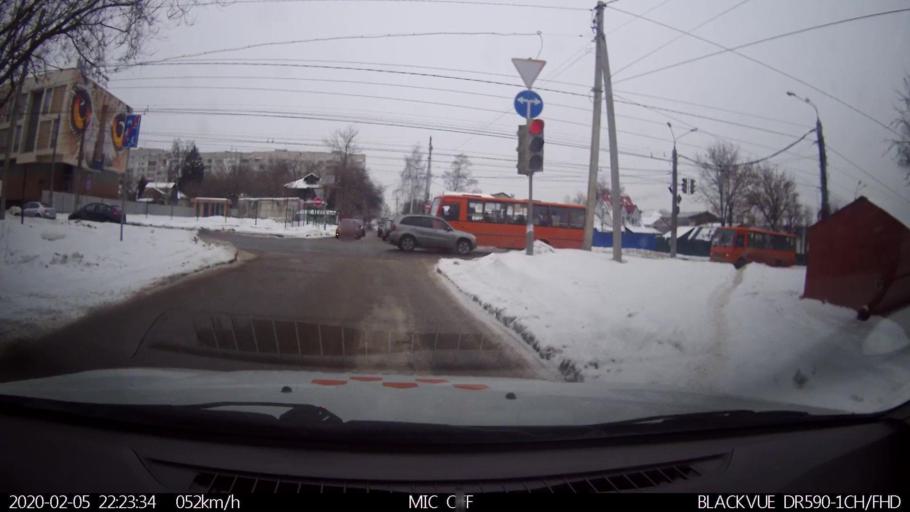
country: RU
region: Nizjnij Novgorod
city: Pervomaysk
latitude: 54.7672
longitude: 44.0393
